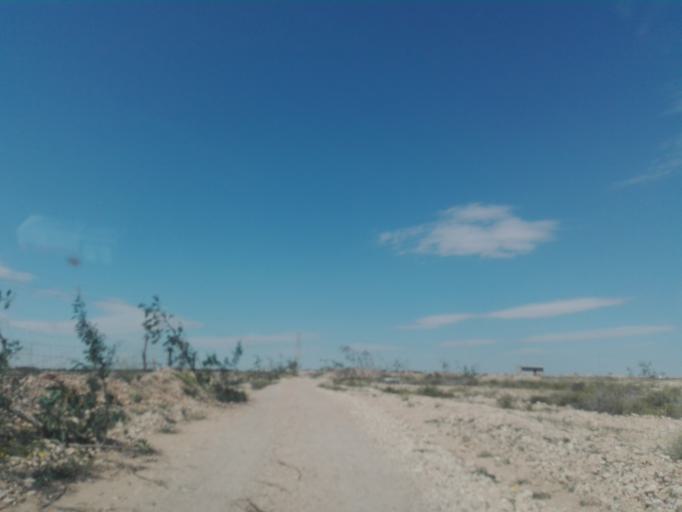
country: TN
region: Safaqis
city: Sfax
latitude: 34.6878
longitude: 10.5405
